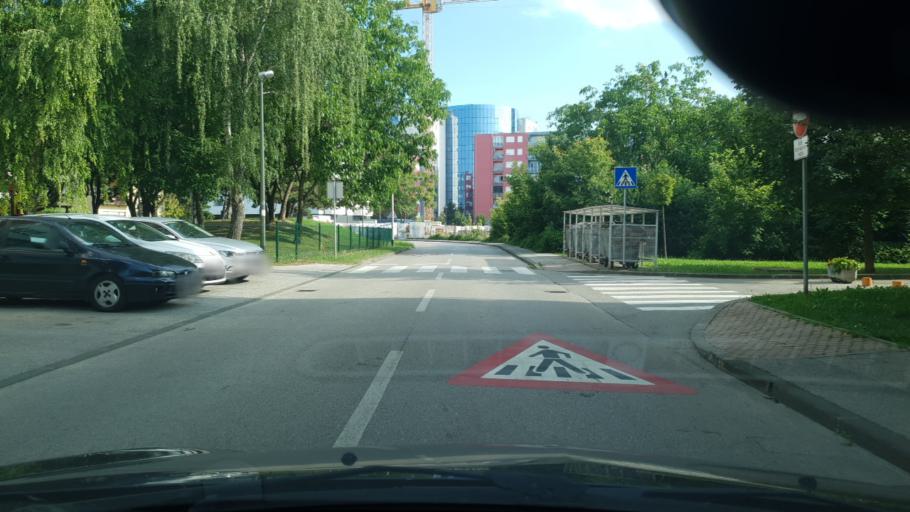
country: HR
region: Grad Zagreb
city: Jankomir
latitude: 45.7934
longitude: 15.9086
